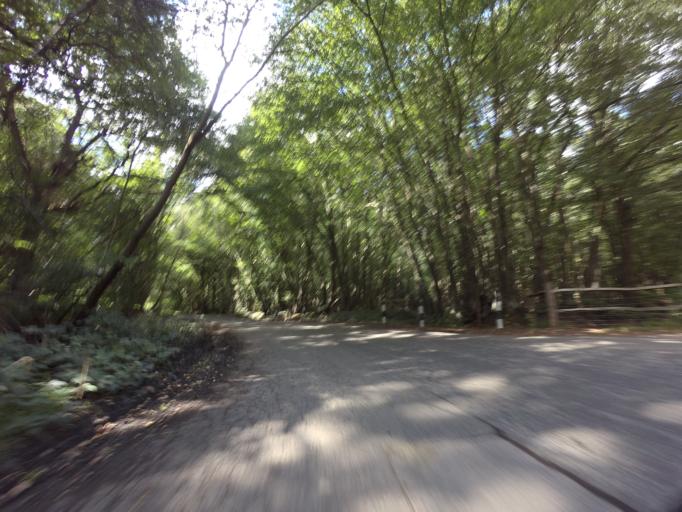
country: GB
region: England
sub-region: Kent
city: Staplehurst
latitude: 51.1343
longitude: 0.5706
